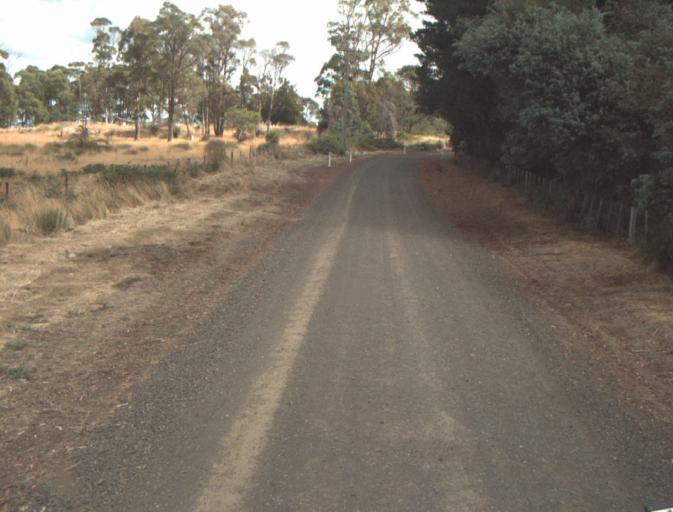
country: AU
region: Tasmania
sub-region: Launceston
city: Mayfield
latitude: -41.2808
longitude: 147.0430
